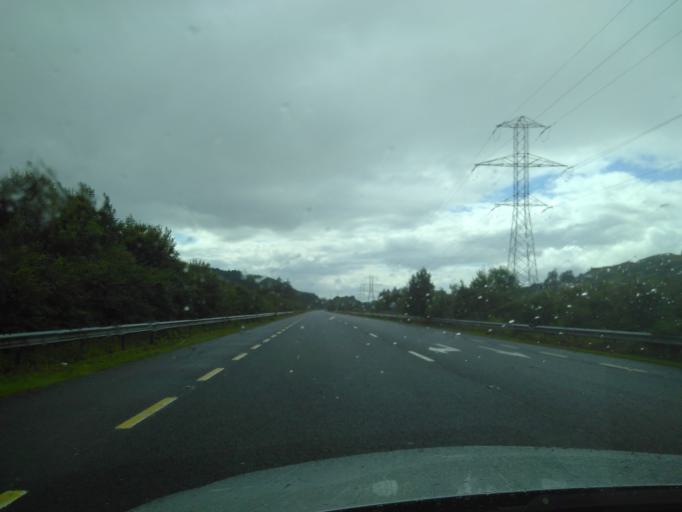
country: IE
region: Ulster
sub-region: County Donegal
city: Donegal
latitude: 54.7085
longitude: -7.9735
